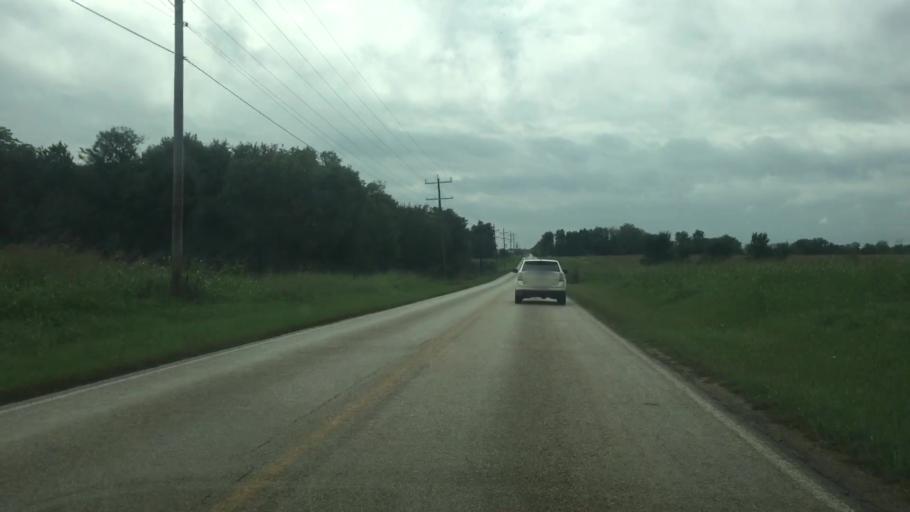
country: US
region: Kansas
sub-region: Allen County
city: Humboldt
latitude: 37.8428
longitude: -95.4369
